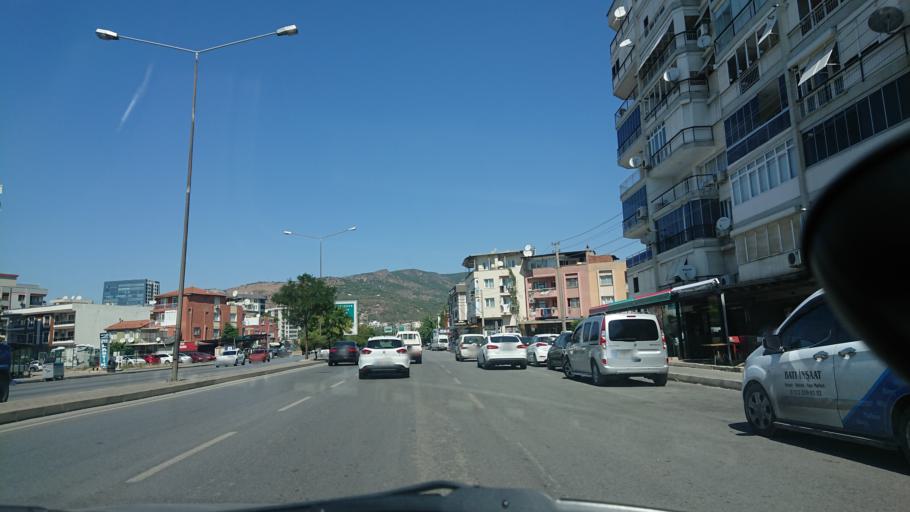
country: TR
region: Izmir
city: Karsiyaka
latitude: 38.4801
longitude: 27.1152
